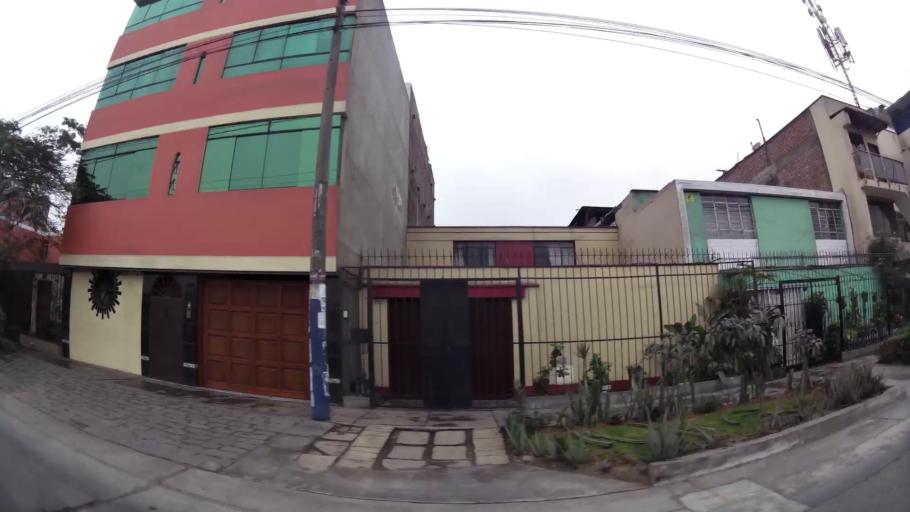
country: PE
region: Lima
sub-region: Lima
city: San Luis
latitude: -12.0791
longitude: -76.9875
